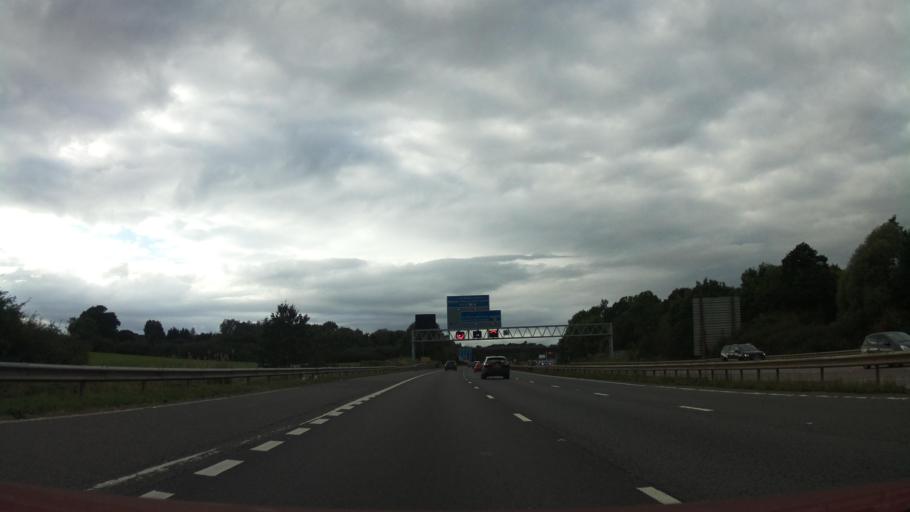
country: GB
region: England
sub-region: Warwickshire
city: Henley in Arden
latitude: 52.3368
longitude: -1.7808
